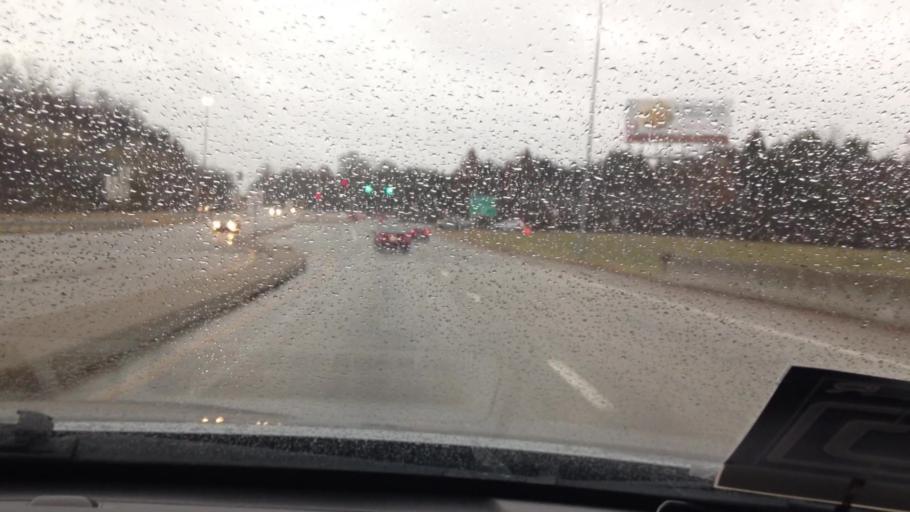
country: US
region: Kansas
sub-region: Johnson County
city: Roeland Park
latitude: 39.0471
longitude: -94.6461
